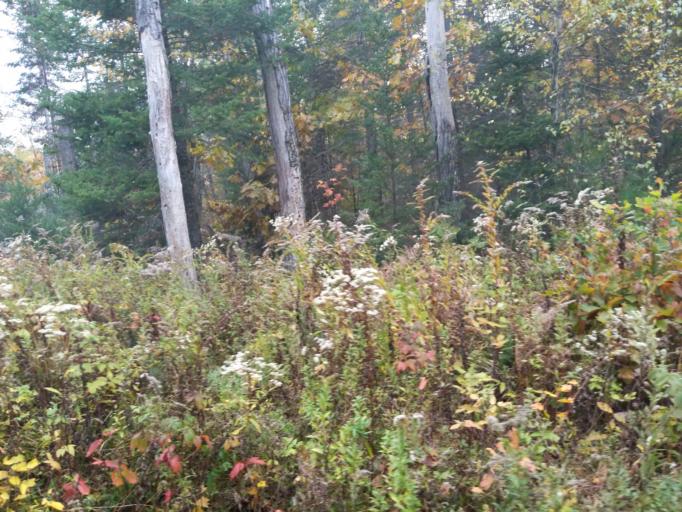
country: US
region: Maine
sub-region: Lincoln County
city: Whitefield
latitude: 44.0941
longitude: -69.6247
